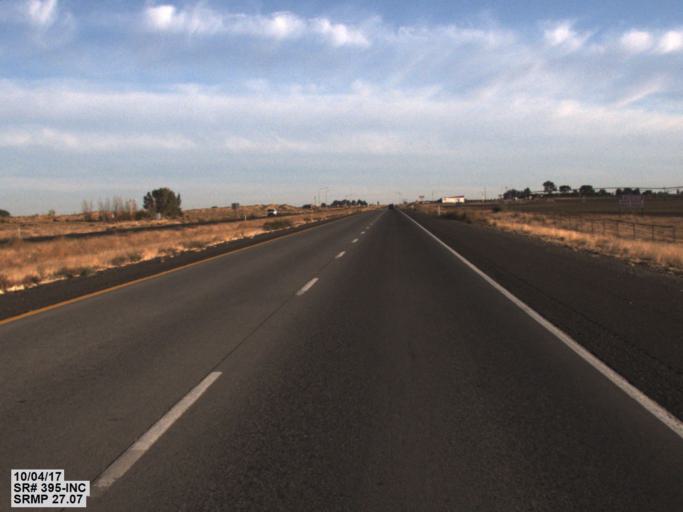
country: US
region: Washington
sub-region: Franklin County
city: Pasco
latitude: 46.3135
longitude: -119.0930
